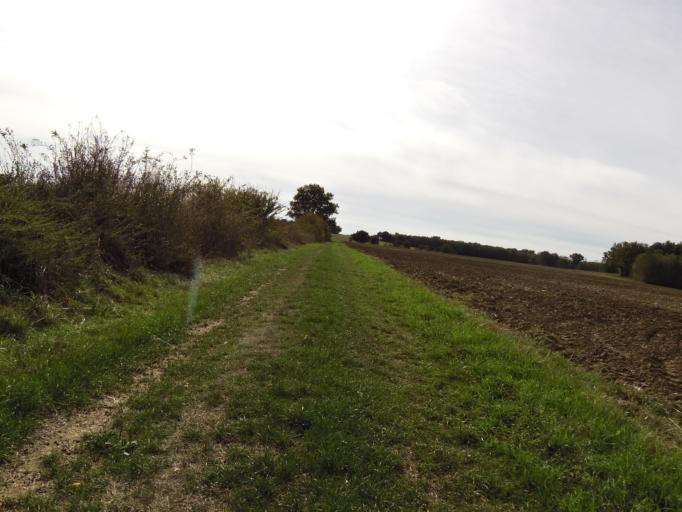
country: FR
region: Rhone-Alpes
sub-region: Departement de l'Ain
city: Perouges
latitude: 45.9347
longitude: 5.1443
